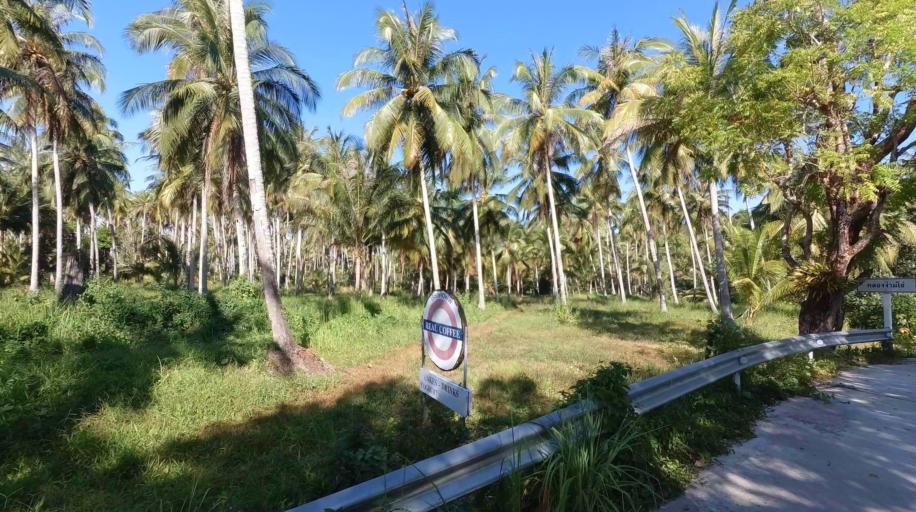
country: TH
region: Trat
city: Ko Kut
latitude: 11.6223
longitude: 102.5508
